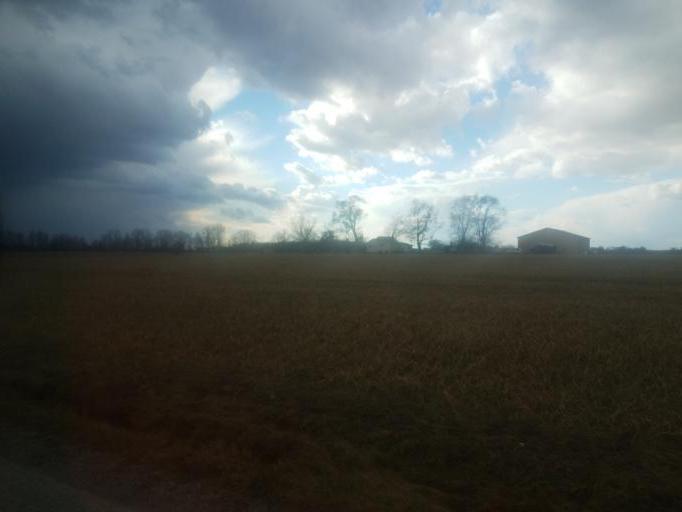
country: US
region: Ohio
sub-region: Marion County
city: Prospect
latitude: 40.4531
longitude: -83.1124
